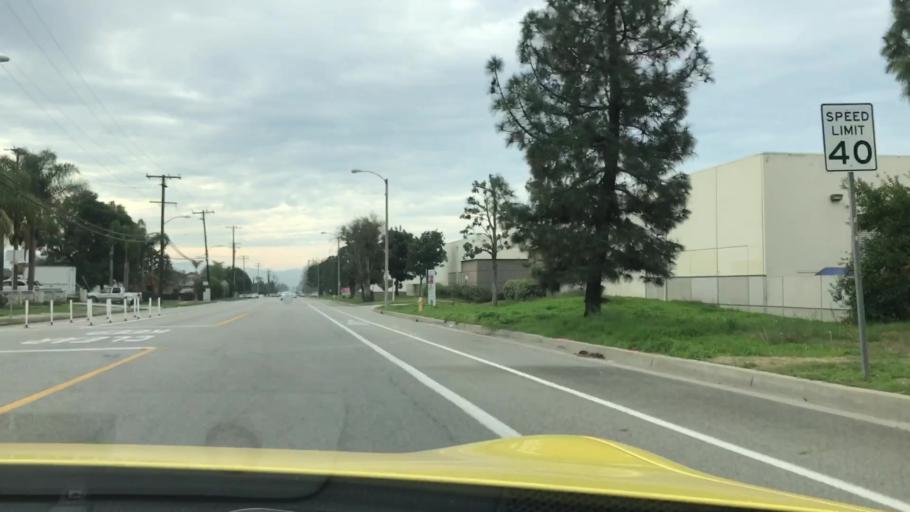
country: US
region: California
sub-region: San Bernardino County
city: Chino
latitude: 34.0111
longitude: -117.6980
